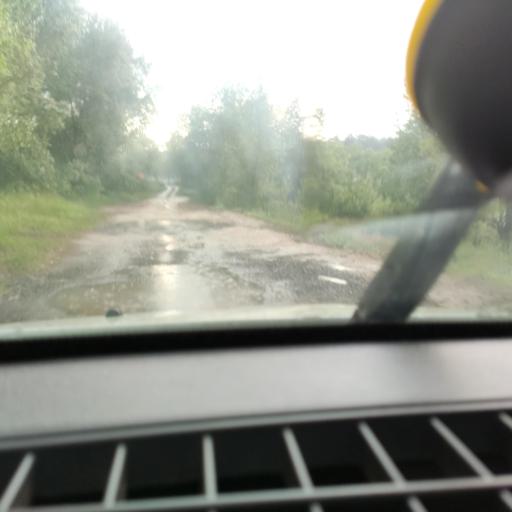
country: RU
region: Samara
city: Zhigulevsk
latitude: 53.5312
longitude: 49.5211
